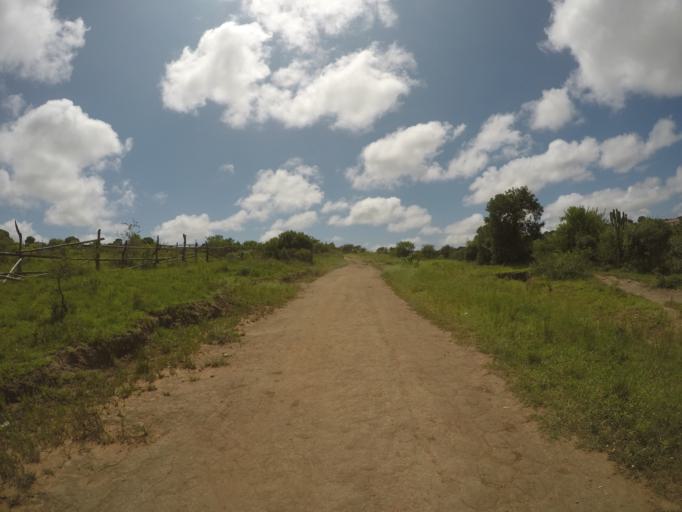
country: ZA
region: KwaZulu-Natal
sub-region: uThungulu District Municipality
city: Empangeni
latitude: -28.5792
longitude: 31.8376
